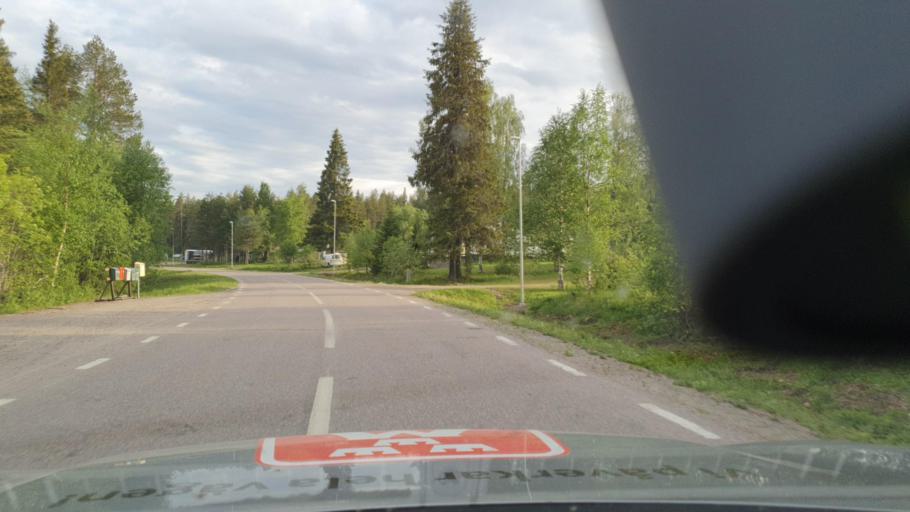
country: SE
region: Norrbotten
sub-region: Gallivare Kommun
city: Gaellivare
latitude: 66.9594
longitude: 21.2356
